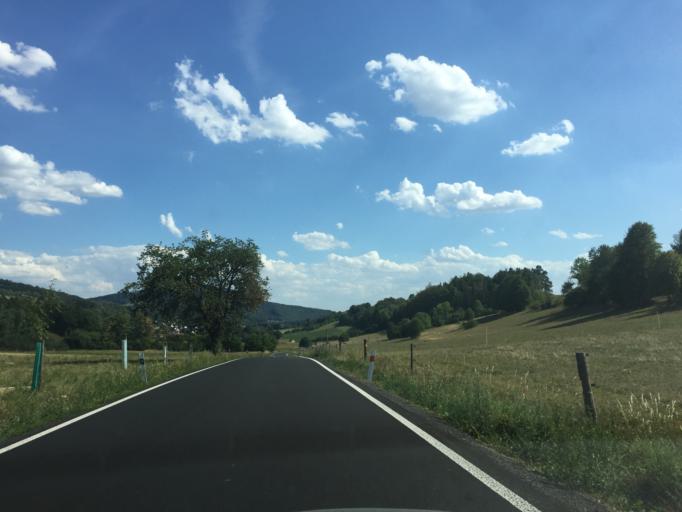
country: CZ
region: Liberecky
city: Mala Skala
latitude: 50.6314
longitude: 15.2148
